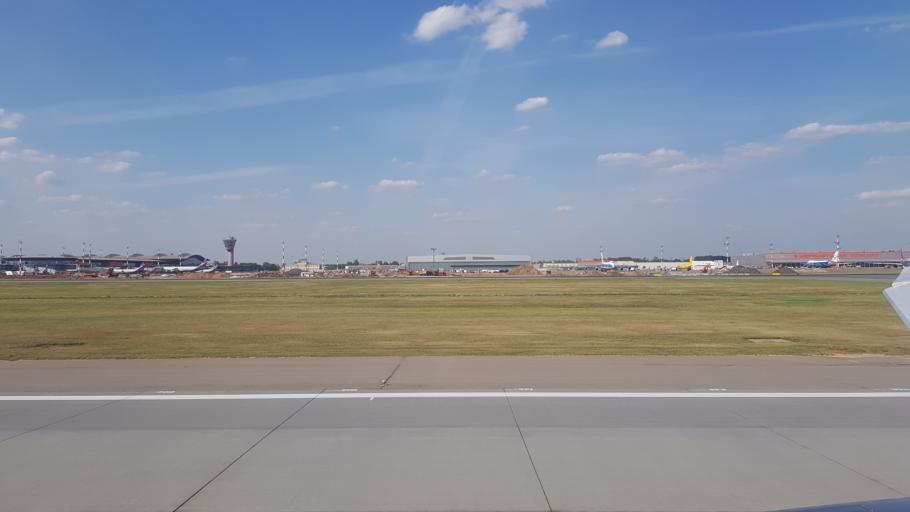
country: RU
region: Moskovskaya
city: Lobnya
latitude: 55.9734
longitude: 37.4277
